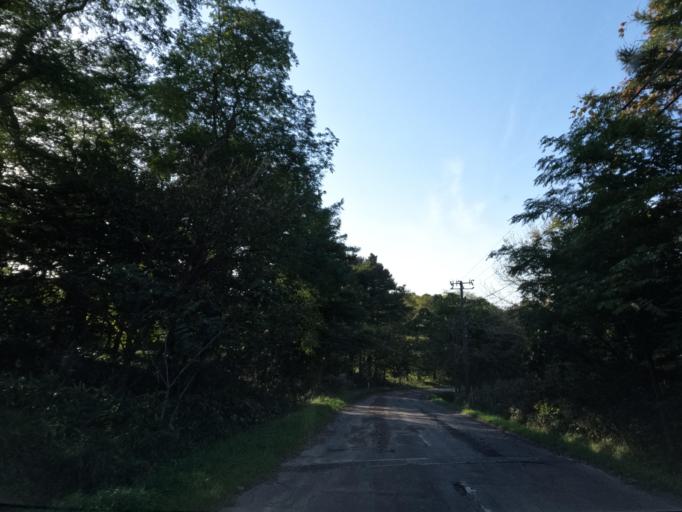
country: JP
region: Hokkaido
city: Date
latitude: 42.3974
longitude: 140.9337
